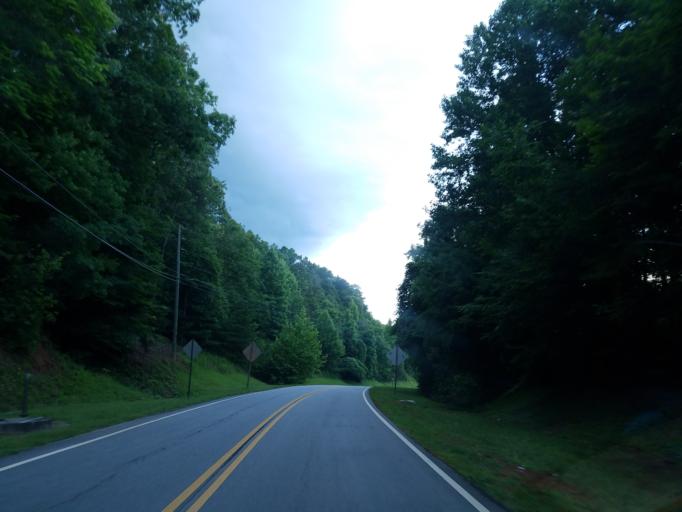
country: US
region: Georgia
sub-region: Lumpkin County
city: Dahlonega
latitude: 34.5471
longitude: -83.9744
